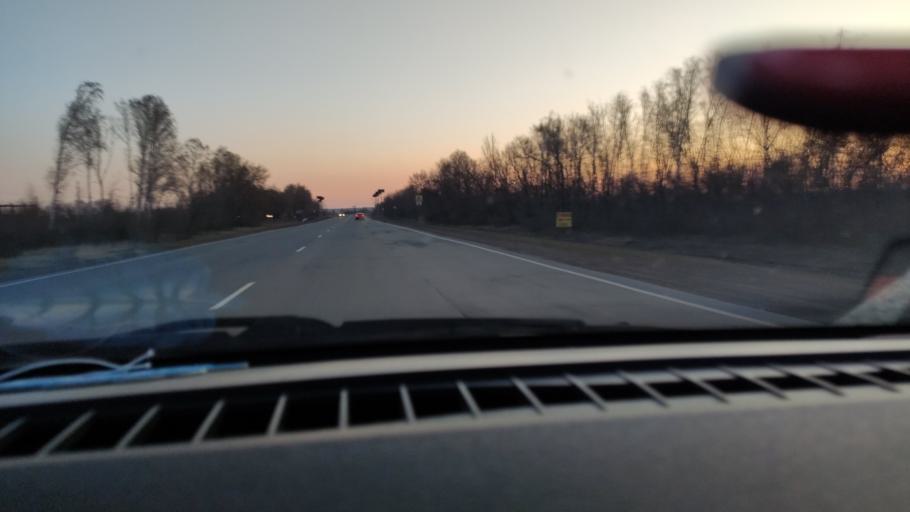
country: RU
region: Saratov
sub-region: Saratovskiy Rayon
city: Saratov
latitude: 51.7022
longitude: 46.0120
